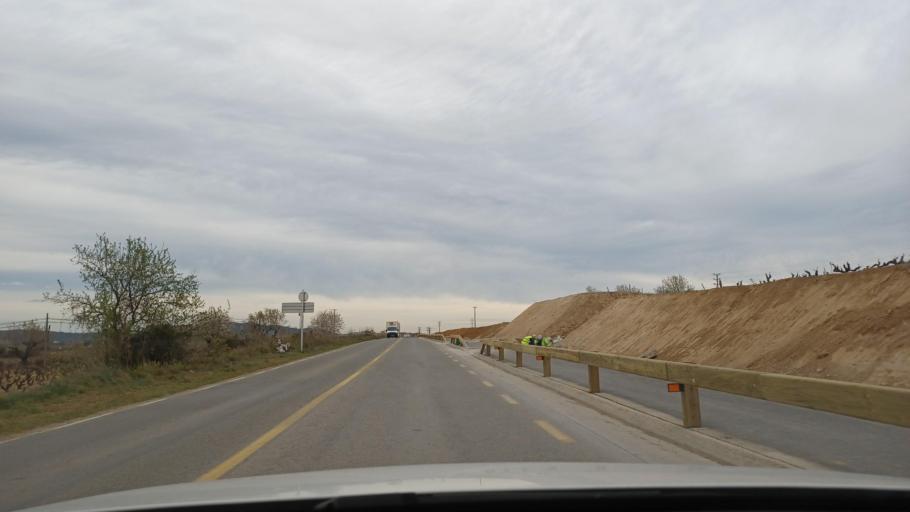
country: ES
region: Catalonia
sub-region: Provincia de Barcelona
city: Vilafranca del Penedes
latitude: 41.3659
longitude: 1.6927
